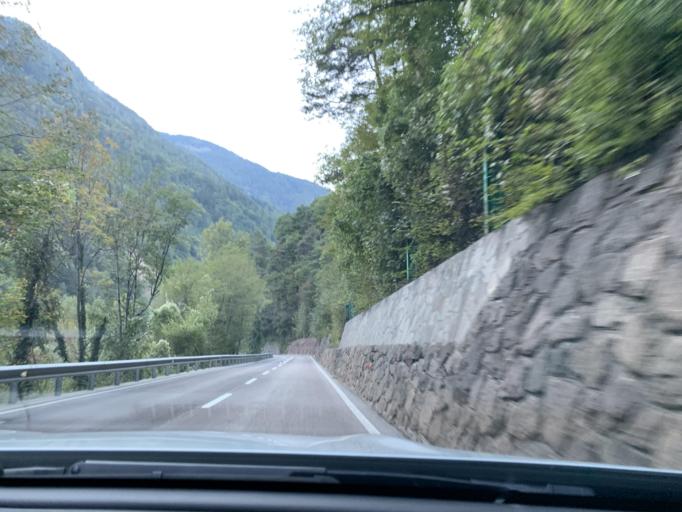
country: IT
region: Trentino-Alto Adige
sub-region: Bolzano
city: Cornedo All'Isarco
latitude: 46.4595
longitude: 11.4204
